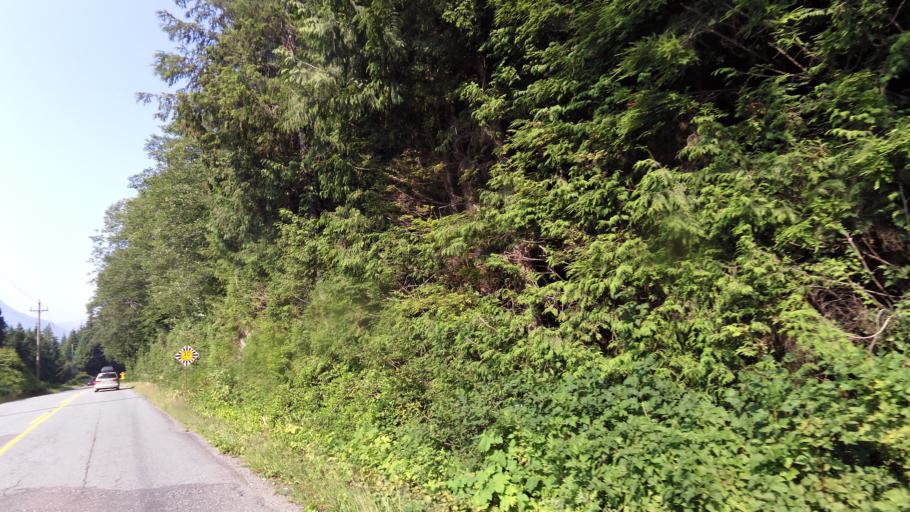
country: CA
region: British Columbia
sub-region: Regional District of Alberni-Clayoquot
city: Ucluelet
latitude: 49.0882
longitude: -125.4572
